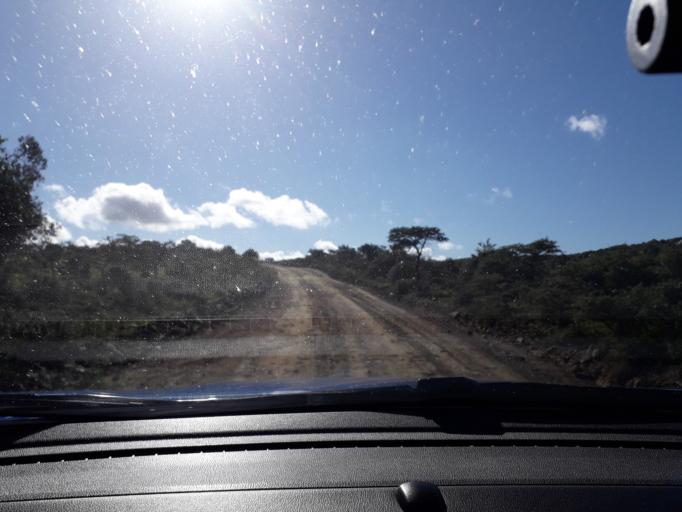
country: ZA
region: Eastern Cape
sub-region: Buffalo City Metropolitan Municipality
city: Bhisho
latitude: -33.1234
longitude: 27.4509
